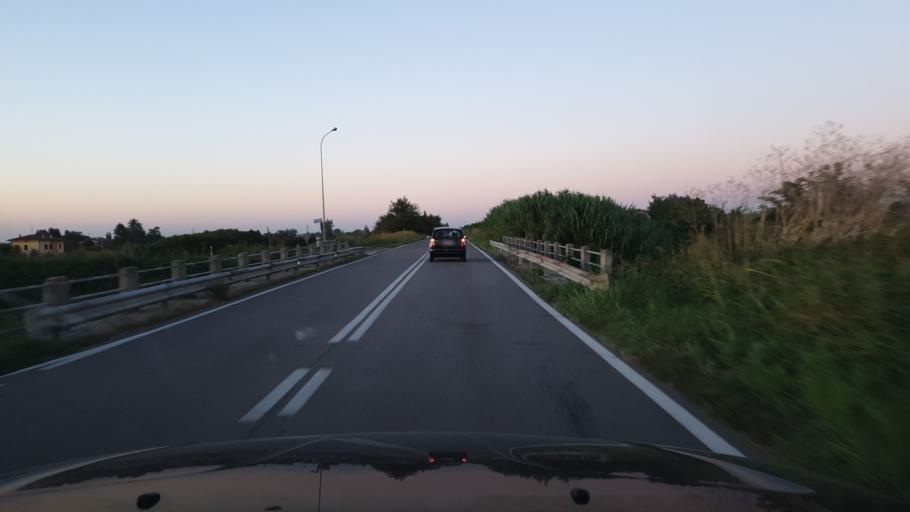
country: IT
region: Emilia-Romagna
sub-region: Provincia di Bologna
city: Minerbio
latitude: 44.6332
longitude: 11.4666
